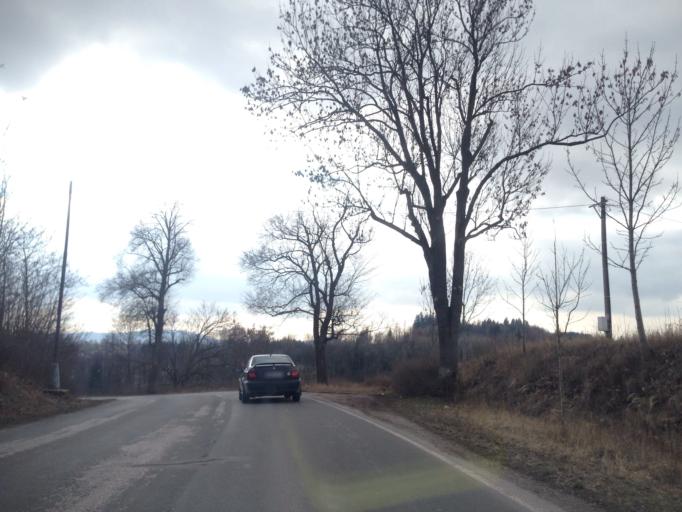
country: CZ
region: Kralovehradecky
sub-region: Okres Trutnov
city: Vrchlabi
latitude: 50.6149
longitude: 15.6042
